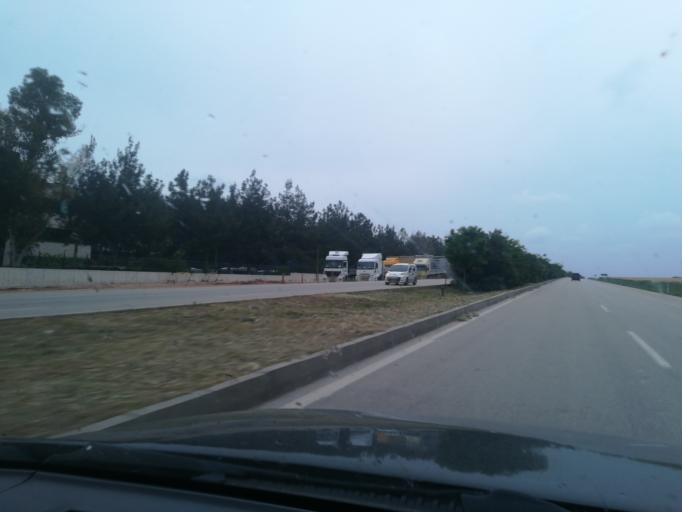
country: TR
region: Adana
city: Yakapinar
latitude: 36.9754
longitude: 35.6510
